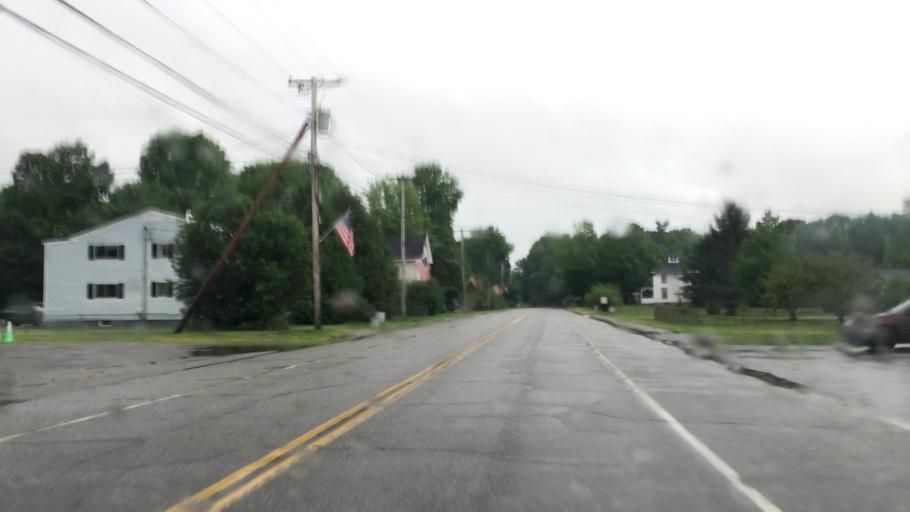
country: US
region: Maine
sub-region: Kennebec County
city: Pittston
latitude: 44.1837
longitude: -69.7569
